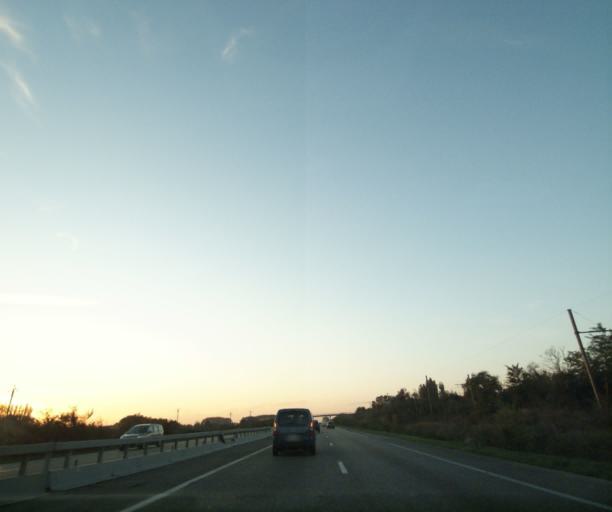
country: FR
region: Provence-Alpes-Cote d'Azur
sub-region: Departement des Bouches-du-Rhone
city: Arles
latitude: 43.6460
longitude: 4.6960
